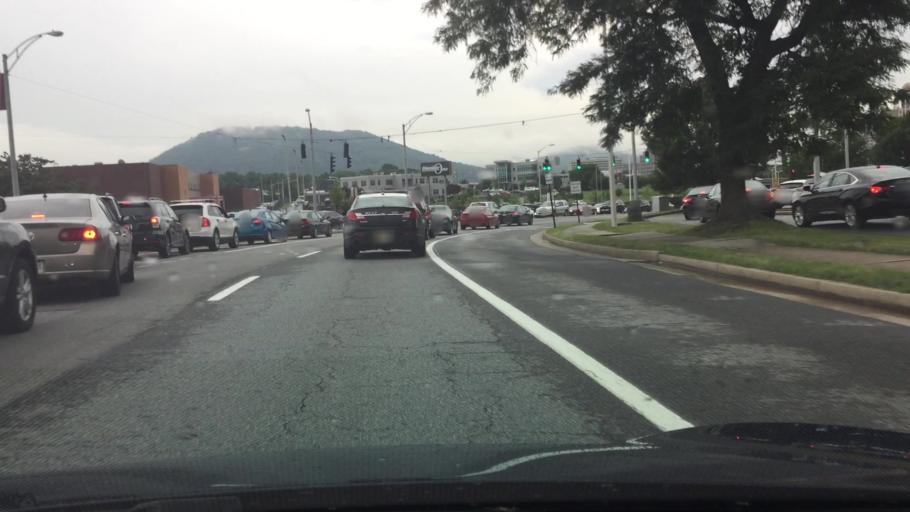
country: US
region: Virginia
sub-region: City of Roanoke
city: Roanoke
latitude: 37.2792
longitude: -79.9344
